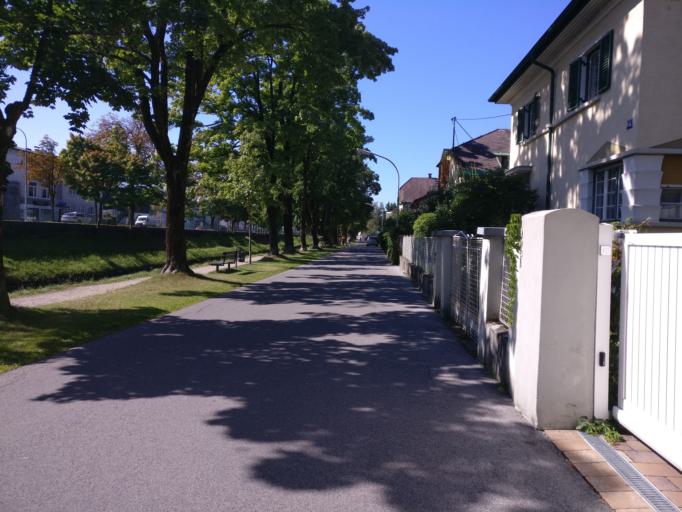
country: AT
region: Carinthia
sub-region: Klagenfurt am Woerthersee
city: Klagenfurt am Woerthersee
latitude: 46.6200
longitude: 14.2762
